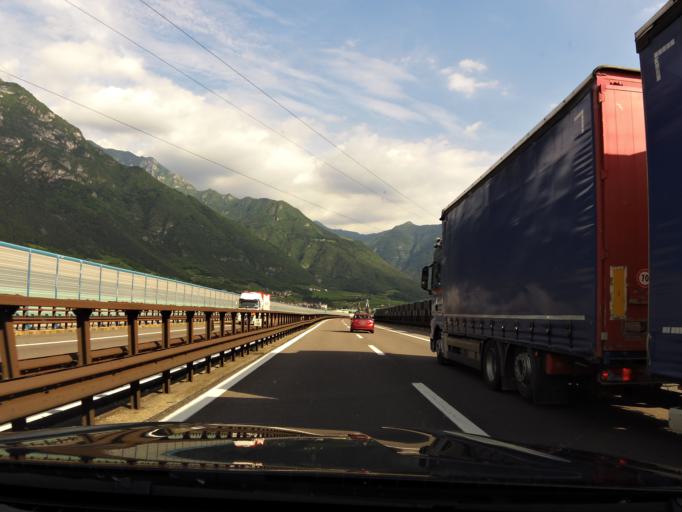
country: IT
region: Trentino-Alto Adige
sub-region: Provincia di Trento
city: Marco
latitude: 45.8087
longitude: 11.0132
